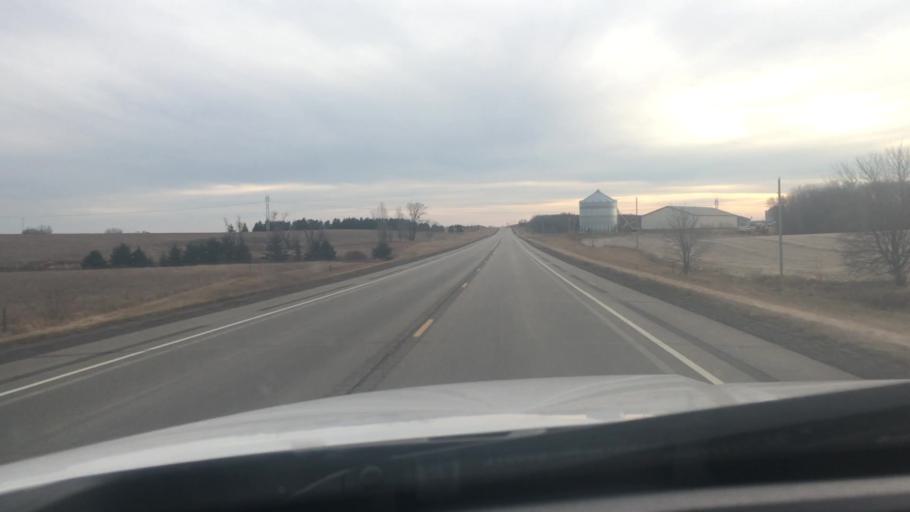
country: US
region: Minnesota
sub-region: Otter Tail County
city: Perham
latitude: 46.3227
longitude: -95.7185
